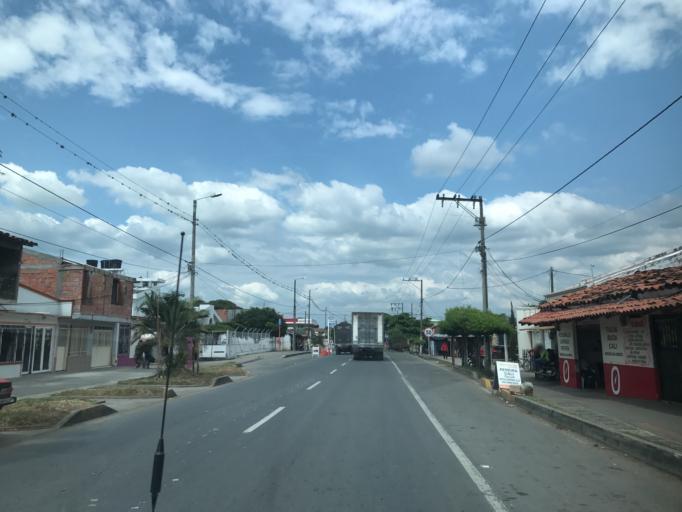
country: CO
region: Valle del Cauca
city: Obando
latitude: 4.5757
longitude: -75.9747
